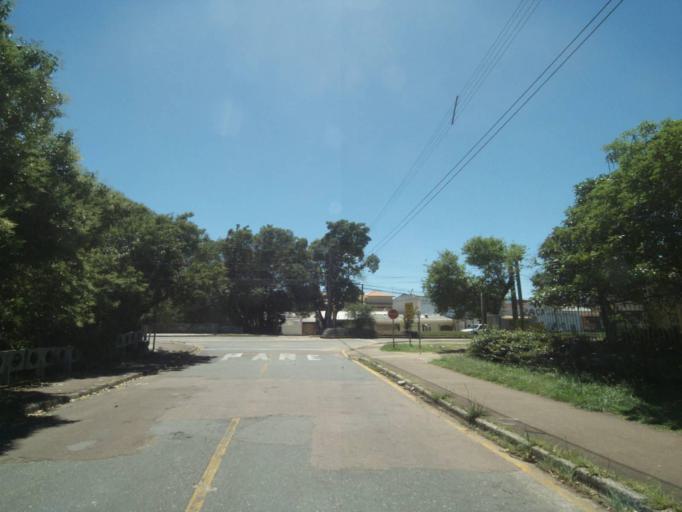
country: BR
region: Parana
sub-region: Curitiba
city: Curitiba
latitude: -25.4745
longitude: -49.3395
